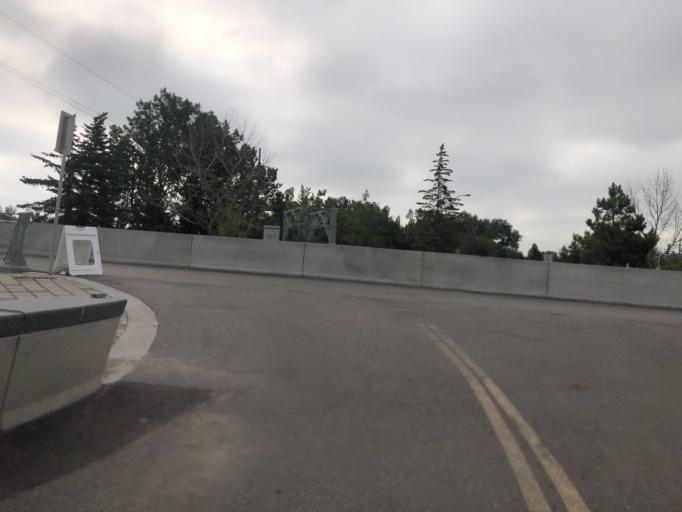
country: CA
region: Alberta
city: Calgary
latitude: 51.0428
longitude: -114.0334
